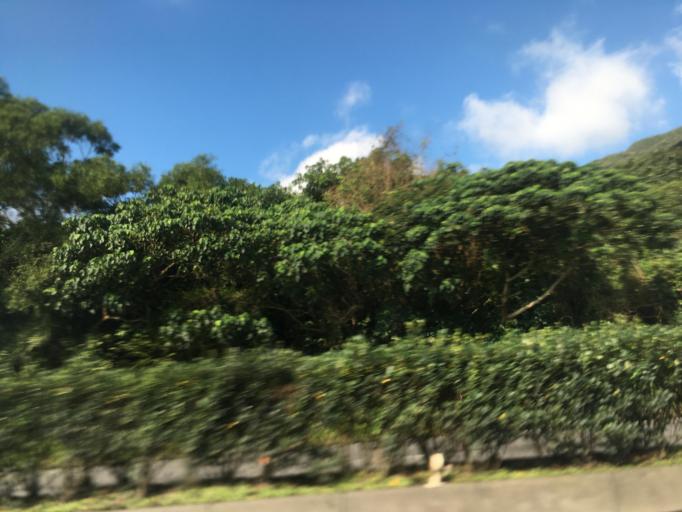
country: TW
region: Taiwan
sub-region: Yilan
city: Yilan
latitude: 24.9324
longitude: 121.8844
